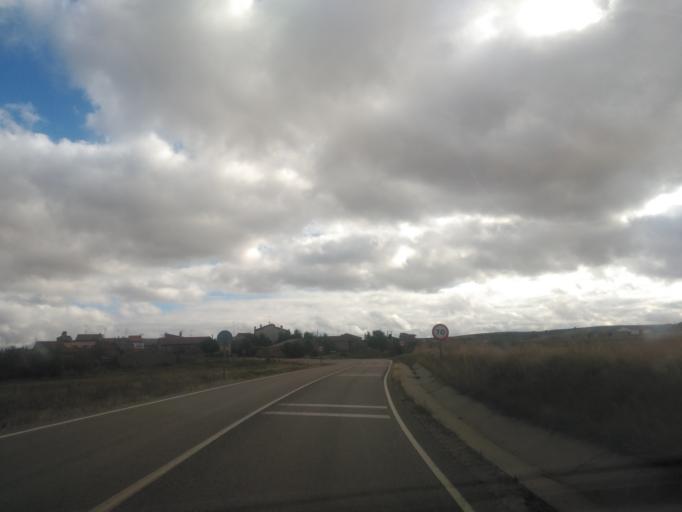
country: ES
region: Castille and Leon
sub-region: Provincia de Soria
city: Espeja de San Marcelino
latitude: 41.7583
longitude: -3.2377
